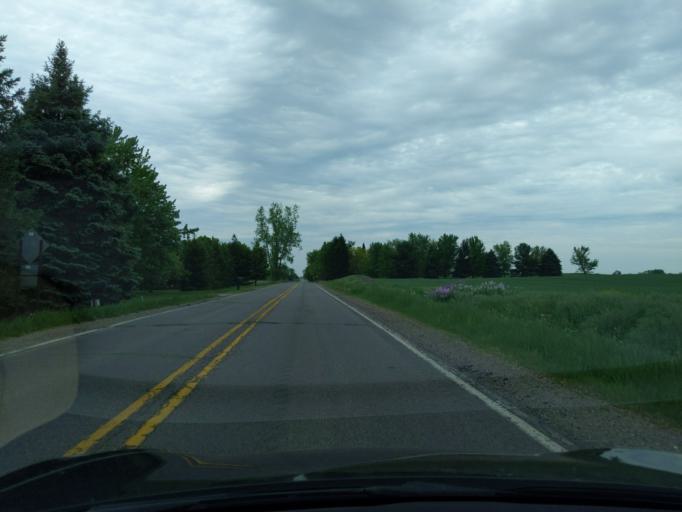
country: US
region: Michigan
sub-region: Ingham County
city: Mason
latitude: 42.6209
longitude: -84.3639
